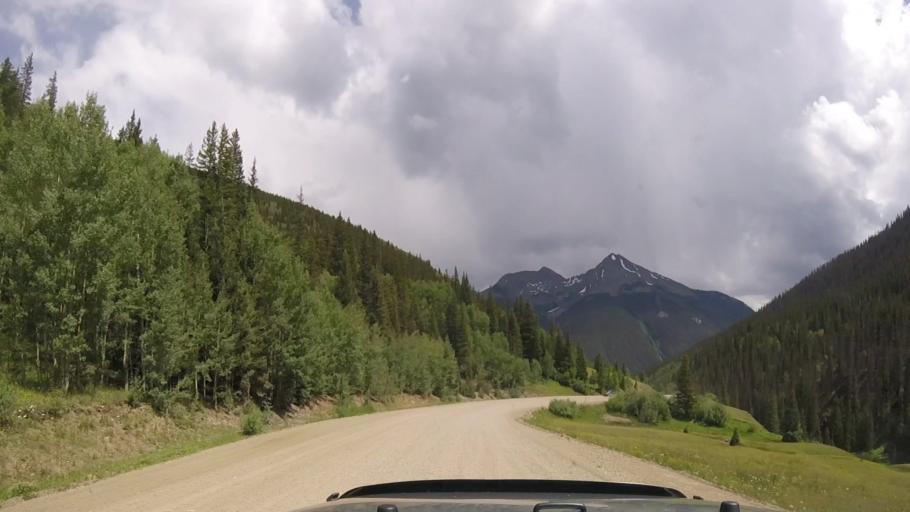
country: US
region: Colorado
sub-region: San Juan County
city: Silverton
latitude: 37.8286
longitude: -107.6698
